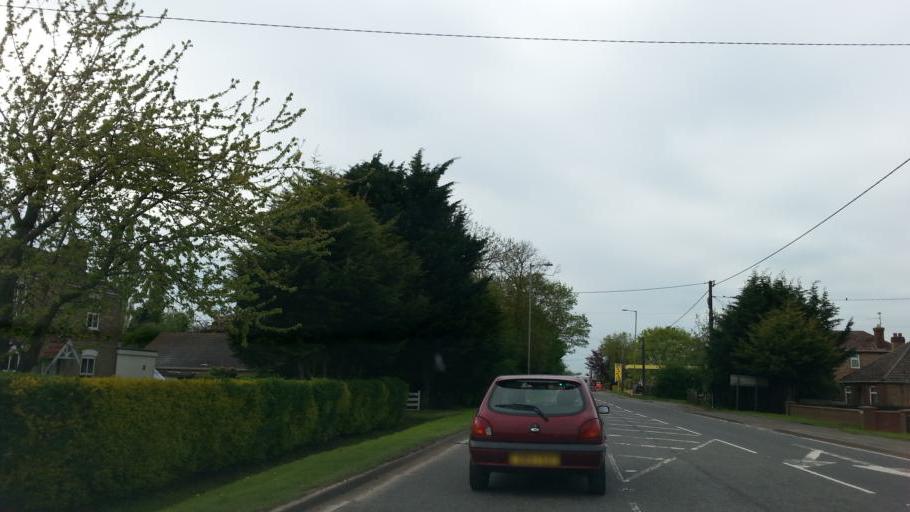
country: GB
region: England
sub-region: Cambridgeshire
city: March
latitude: 52.5683
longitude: 0.0607
